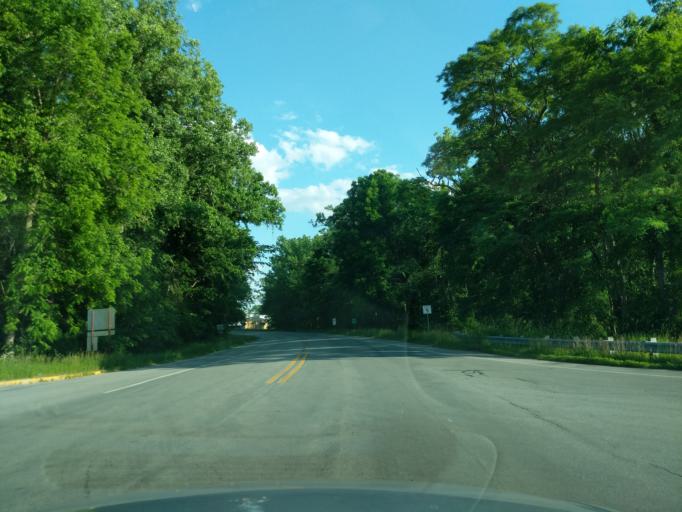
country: US
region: Indiana
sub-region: Whitley County
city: Columbia City
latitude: 41.1471
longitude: -85.4883
